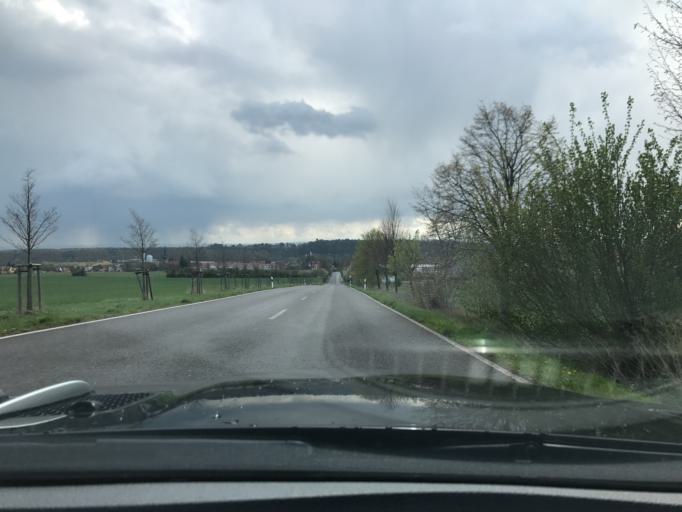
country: DE
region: Thuringia
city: Muehlhausen
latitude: 51.2193
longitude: 10.4920
